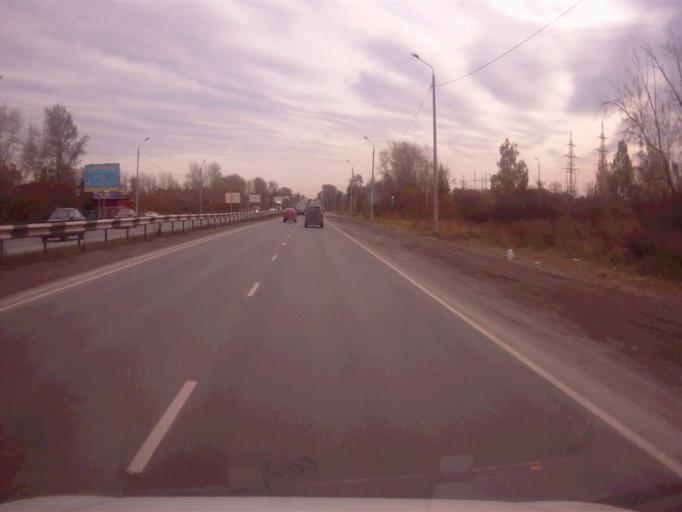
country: RU
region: Chelyabinsk
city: Novosineglazovskiy
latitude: 55.0615
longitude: 61.4007
